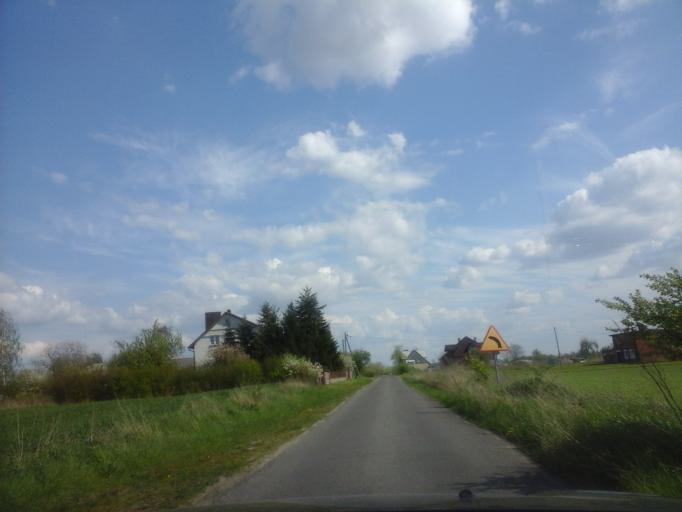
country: PL
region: West Pomeranian Voivodeship
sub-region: Powiat choszczenski
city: Krzecin
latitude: 53.1292
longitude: 15.4662
